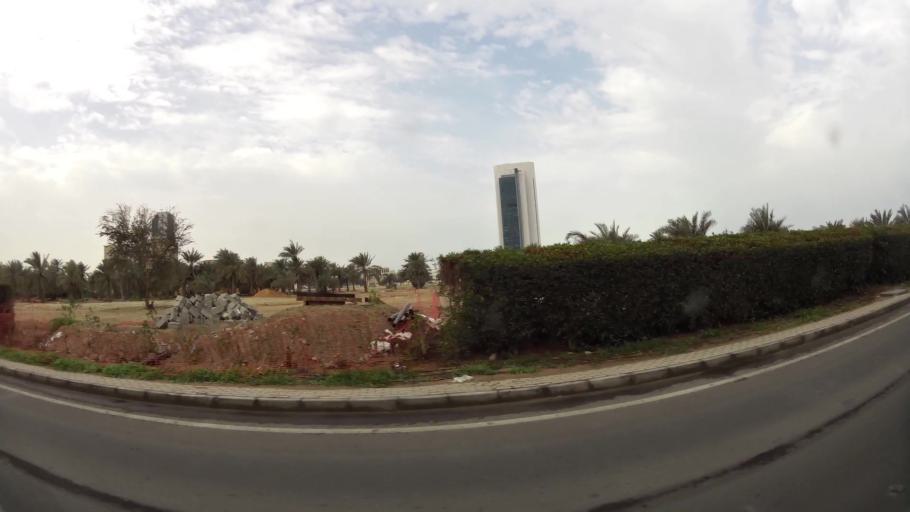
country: AE
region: Abu Dhabi
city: Abu Dhabi
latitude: 24.4621
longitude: 54.3987
